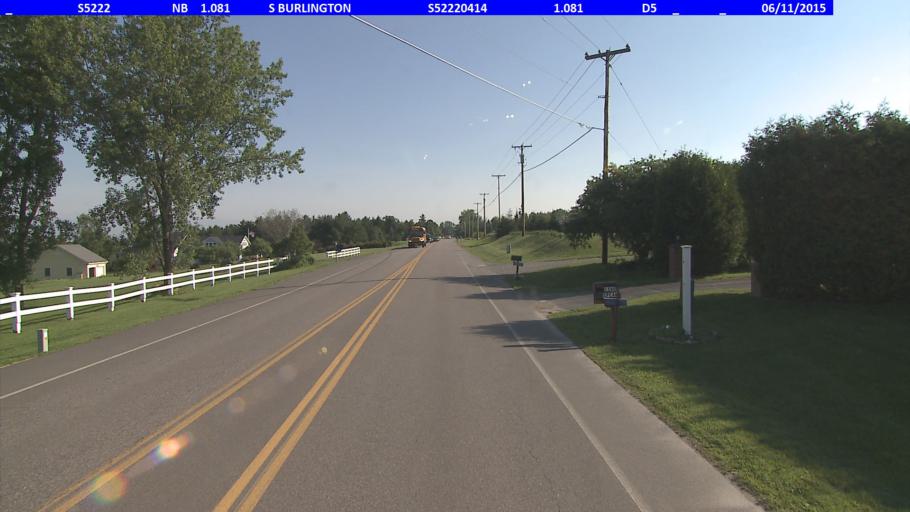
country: US
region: Vermont
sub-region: Chittenden County
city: South Burlington
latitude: 44.4323
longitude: -73.1926
